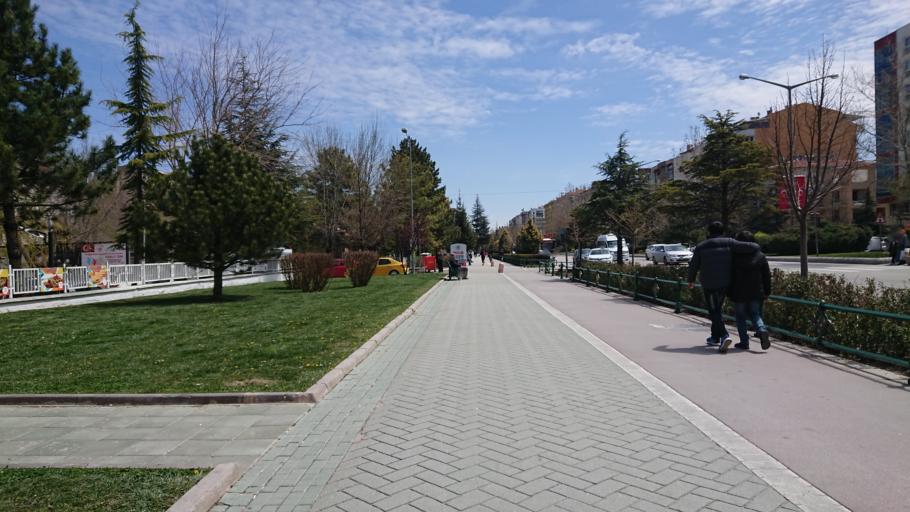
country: TR
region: Eskisehir
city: Eskisehir
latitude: 39.7653
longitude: 30.5115
